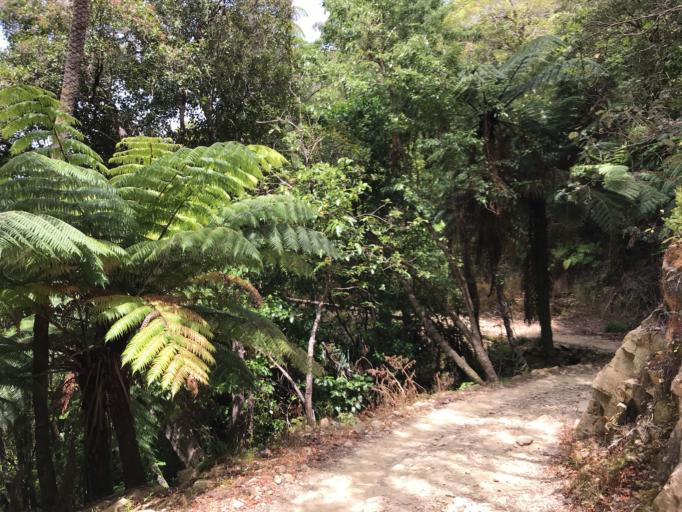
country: NZ
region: Marlborough
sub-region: Marlborough District
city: Picton
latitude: -41.1210
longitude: 174.1915
